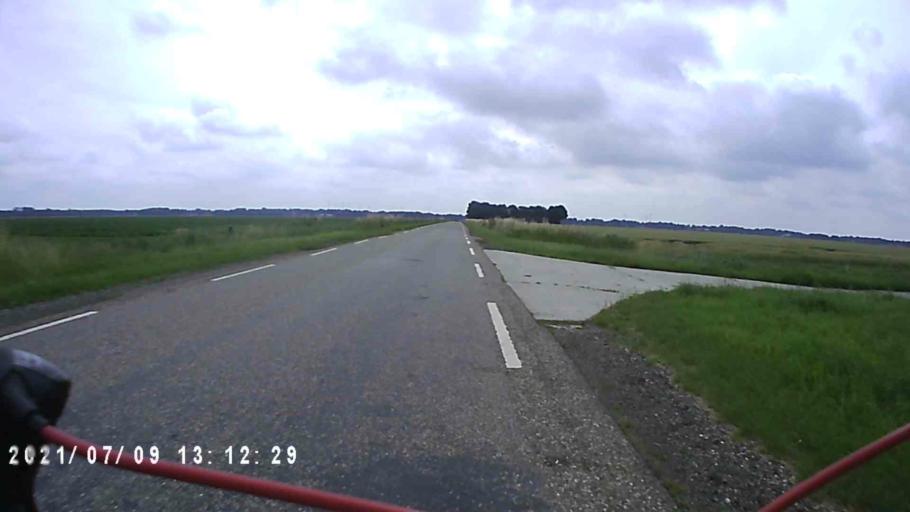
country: NL
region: Groningen
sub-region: Gemeente Vlagtwedde
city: Vlagtwedde
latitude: 53.1240
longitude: 7.1364
